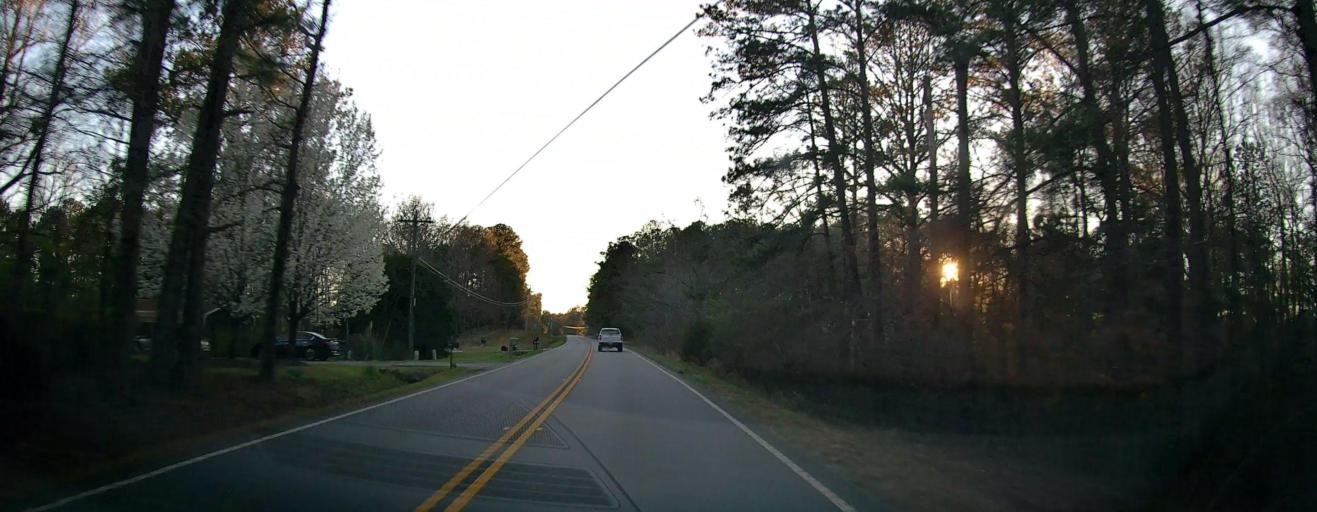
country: US
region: Alabama
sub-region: Lee County
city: Smiths Station
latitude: 32.6378
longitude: -85.0276
